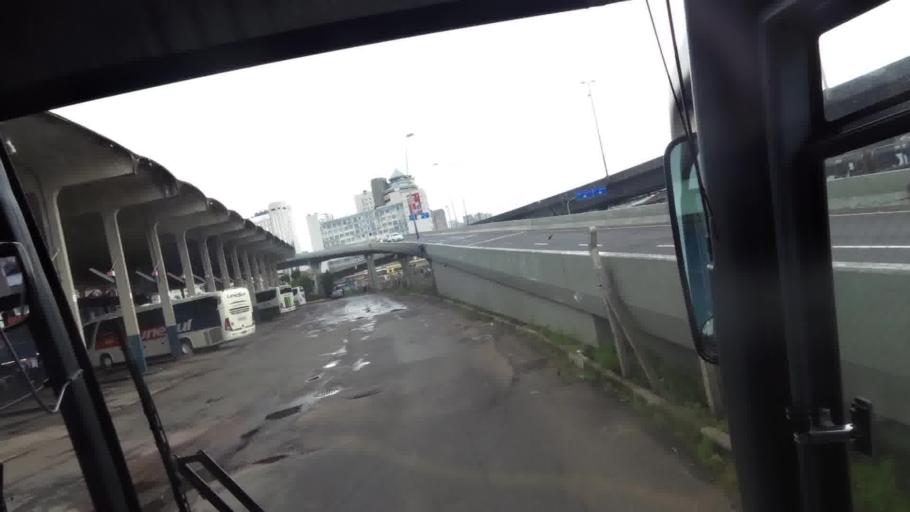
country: BR
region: Rio Grande do Sul
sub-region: Porto Alegre
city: Porto Alegre
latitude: -30.0221
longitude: -51.2193
